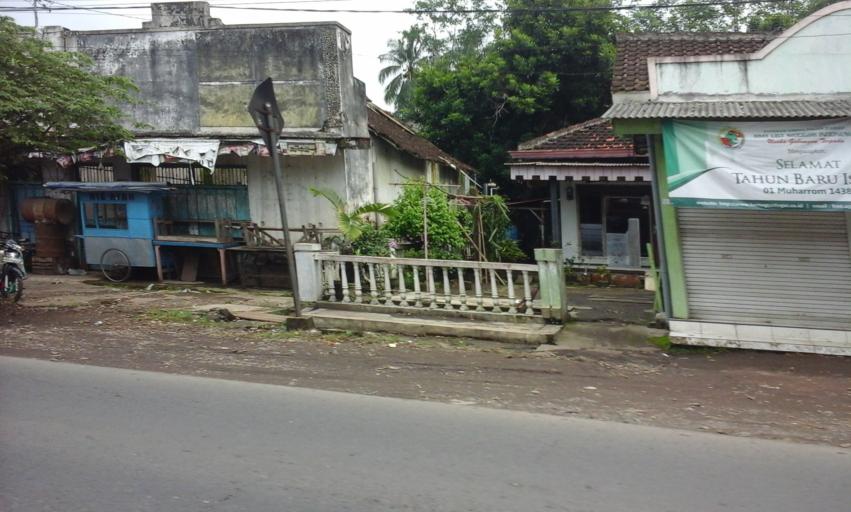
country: ID
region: East Java
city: Klatakan
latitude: -8.1927
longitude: 113.5024
